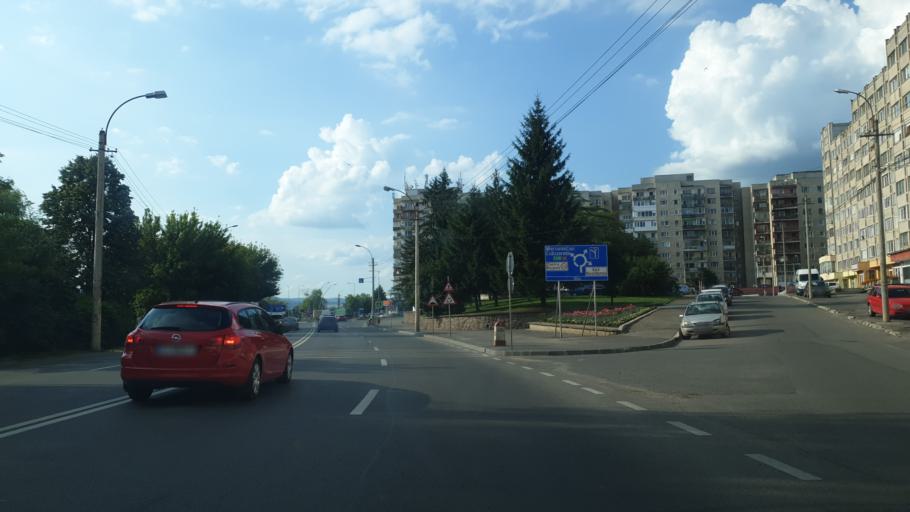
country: RO
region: Covasna
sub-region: Municipiul Sfantu Gheorghe
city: Sfantu-Gheorghe
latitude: 45.8617
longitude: 25.8076
